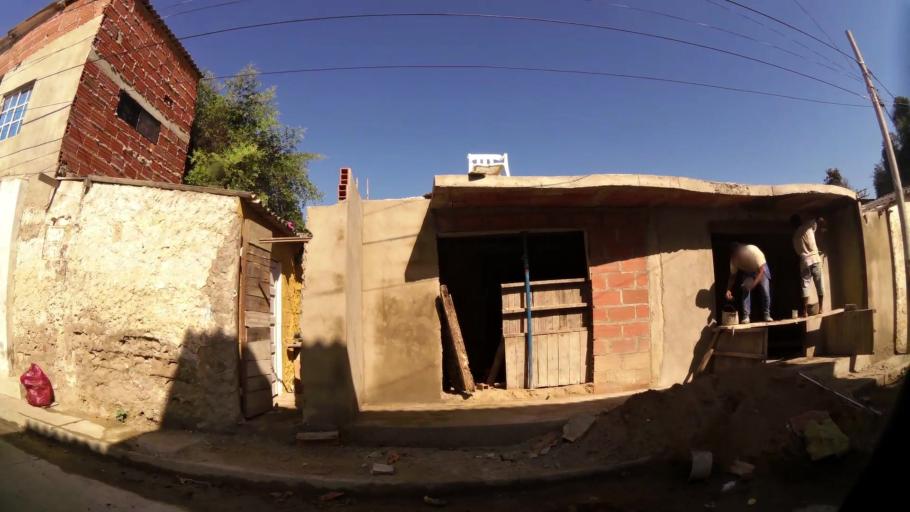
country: CO
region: Bolivar
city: Cartagena
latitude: 10.4272
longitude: -75.5324
